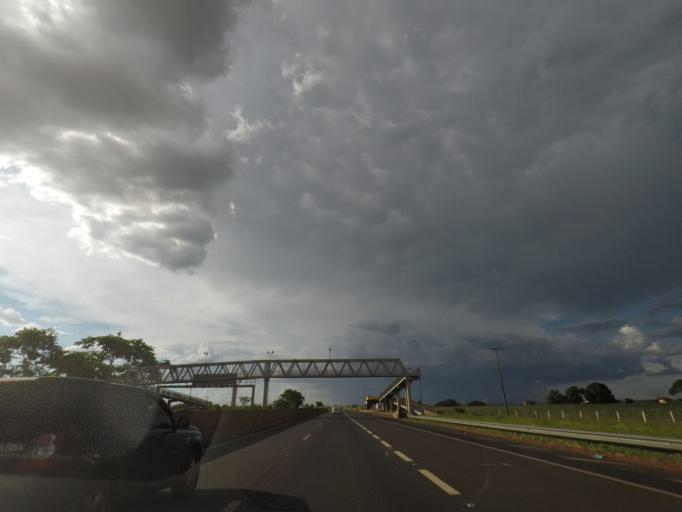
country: BR
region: Sao Paulo
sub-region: Jardinopolis
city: Jardinopolis
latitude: -21.0886
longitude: -47.7974
